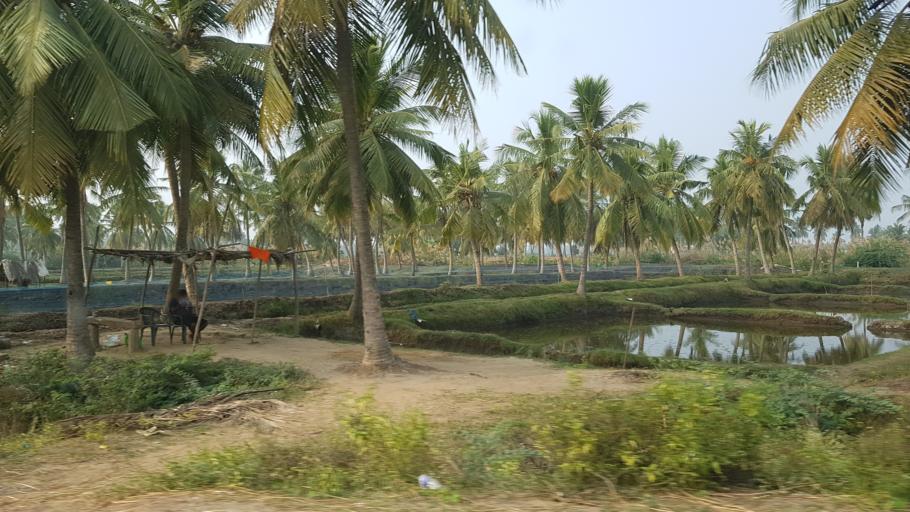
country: IN
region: Andhra Pradesh
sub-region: Krishna
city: Pallevada
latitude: 16.5199
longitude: 81.3336
